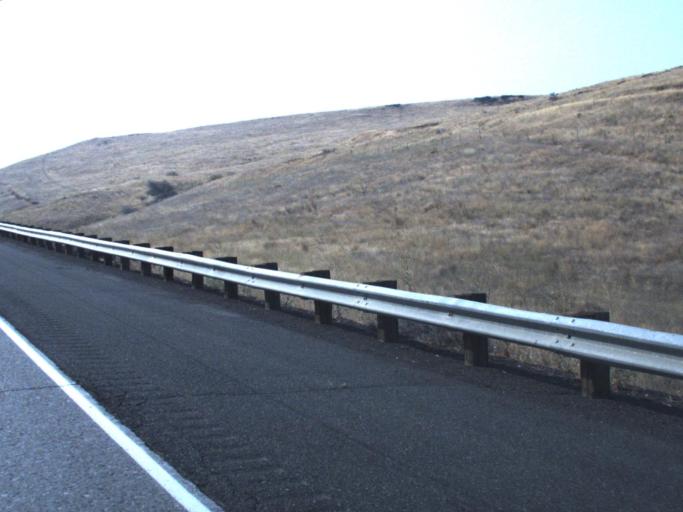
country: US
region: Washington
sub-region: Yakima County
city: Terrace Heights
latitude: 46.7398
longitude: -120.3876
